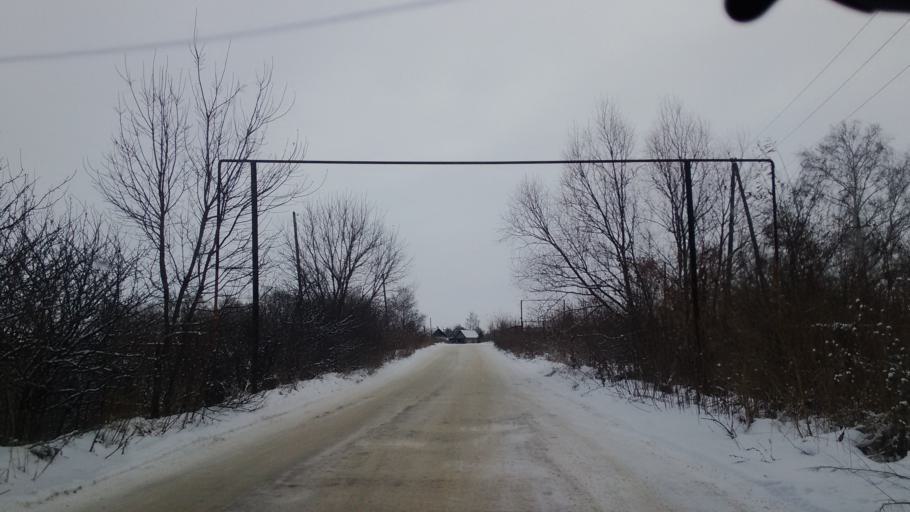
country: RU
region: Tula
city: Bogoroditsk
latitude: 53.7593
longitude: 38.1072
